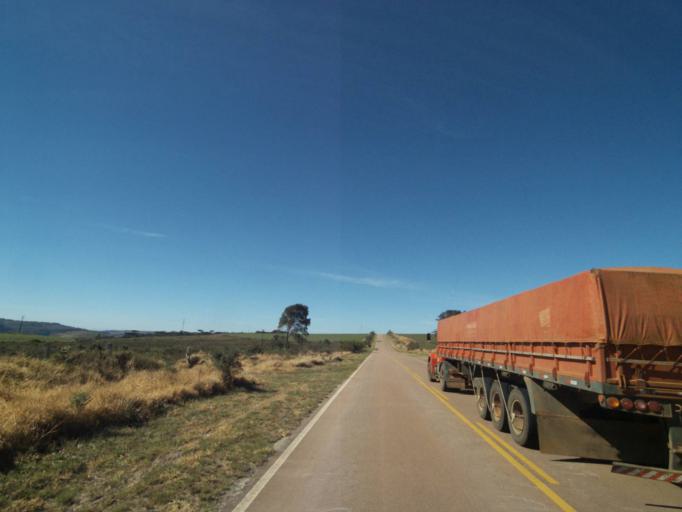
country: BR
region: Parana
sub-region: Tibagi
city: Tibagi
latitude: -24.6294
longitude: -50.2427
